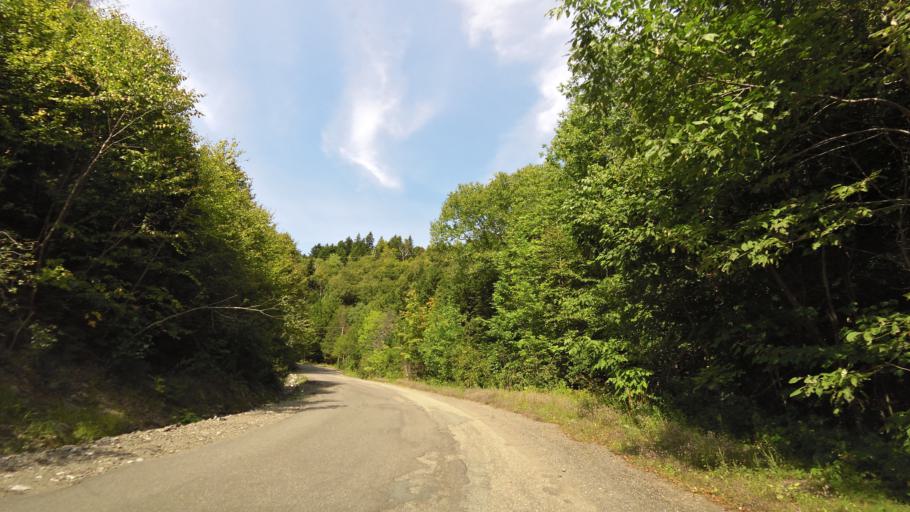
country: CA
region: New Brunswick
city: Hampton
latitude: 45.5511
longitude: -65.8379
